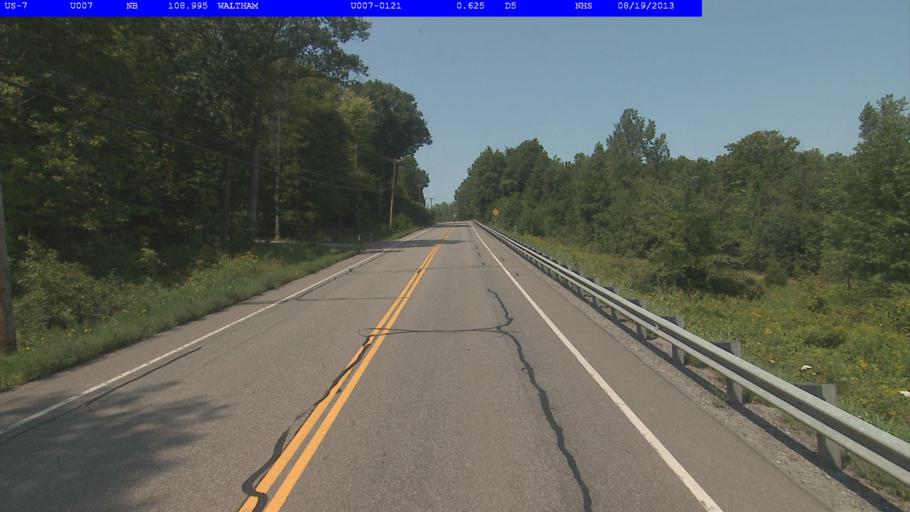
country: US
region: Vermont
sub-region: Addison County
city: Vergennes
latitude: 44.1544
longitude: -73.2186
